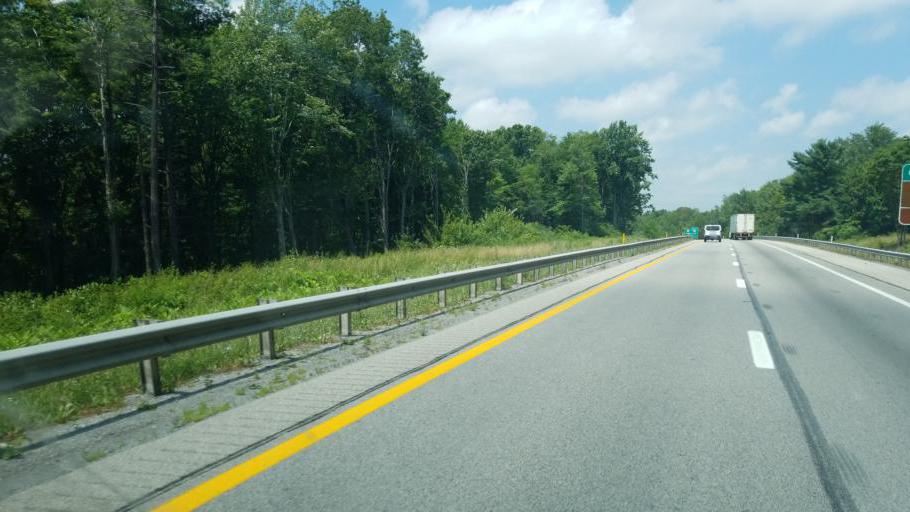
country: US
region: West Virginia
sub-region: Mercer County
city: Athens
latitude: 37.4115
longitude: -81.0615
